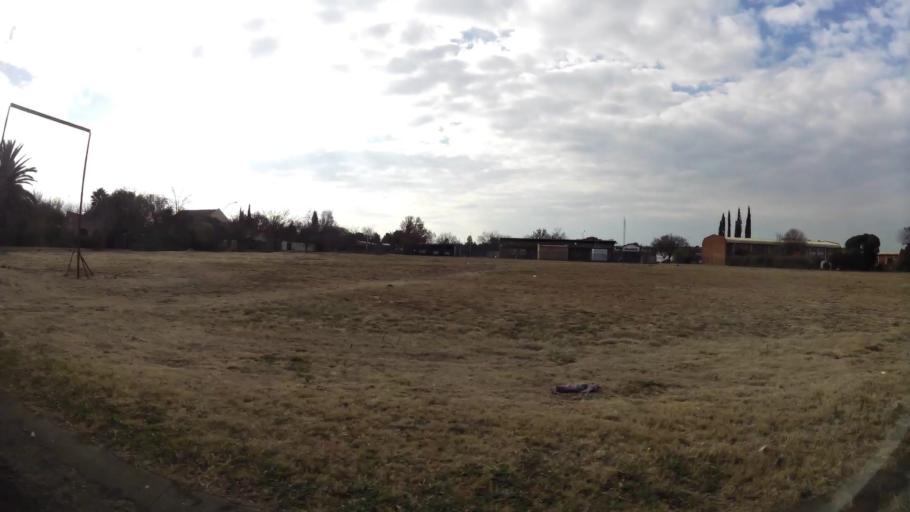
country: ZA
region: Orange Free State
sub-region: Mangaung Metropolitan Municipality
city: Bloemfontein
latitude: -29.0859
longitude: 26.2426
